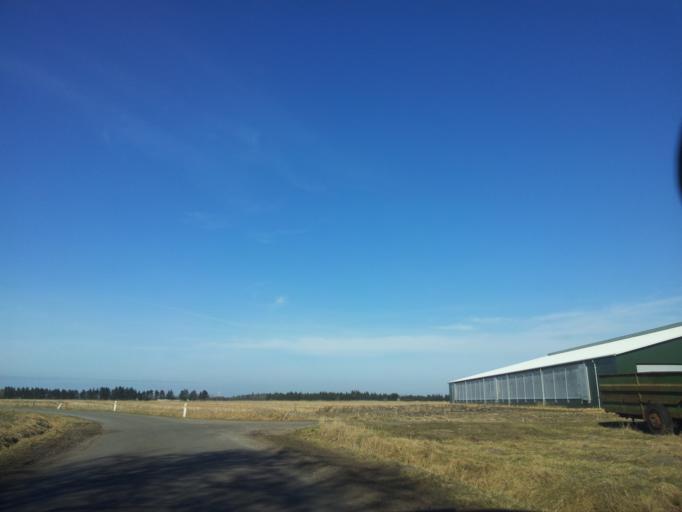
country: DK
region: South Denmark
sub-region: Tonder Kommune
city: Sherrebek
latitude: 55.1747
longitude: 8.7214
